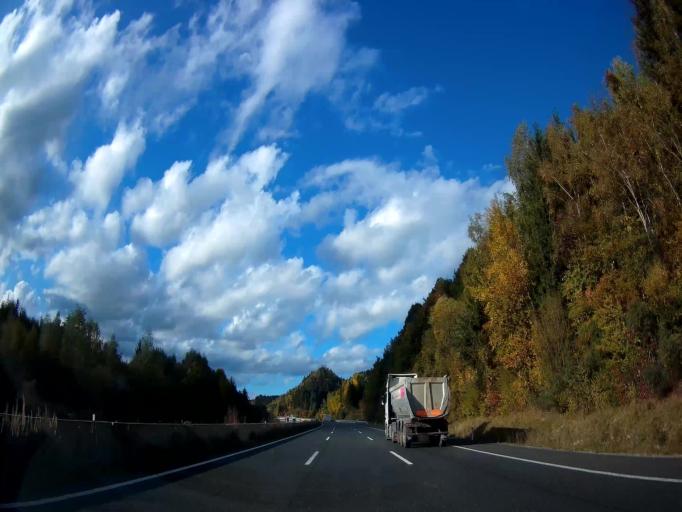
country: AT
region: Carinthia
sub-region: Politischer Bezirk Wolfsberg
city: Wolfsberg
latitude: 46.8820
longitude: 14.8301
